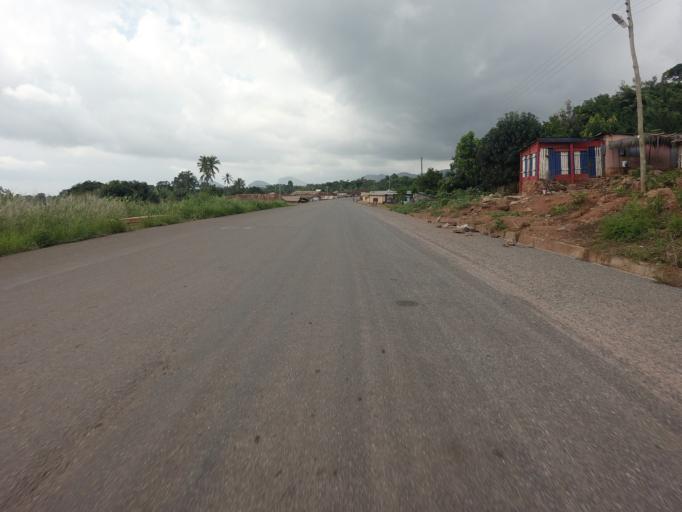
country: GH
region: Volta
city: Kpandu
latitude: 6.9119
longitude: 0.4486
